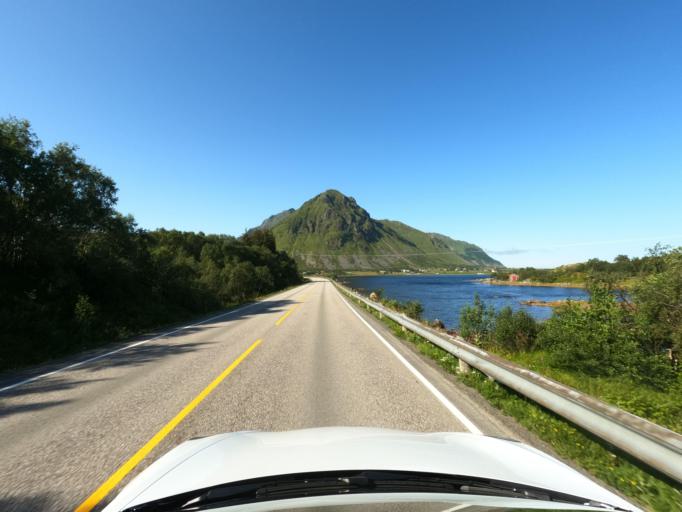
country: NO
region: Nordland
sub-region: Vestvagoy
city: Evjen
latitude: 68.2650
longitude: 13.9794
